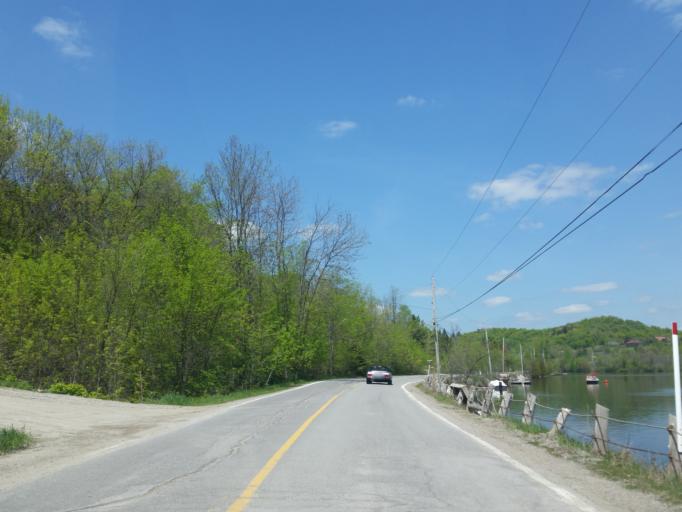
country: CA
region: Quebec
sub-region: Outaouais
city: Wakefield
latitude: 45.5968
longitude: -75.8817
